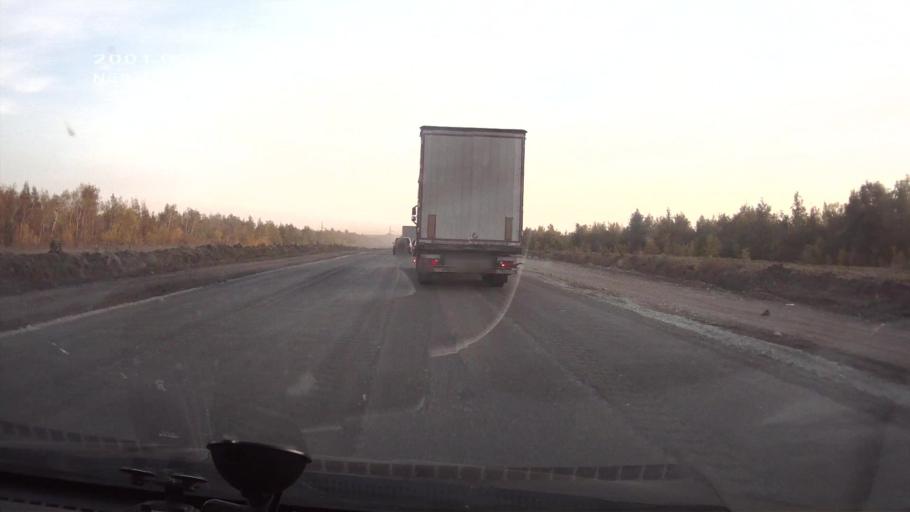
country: RU
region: Saratov
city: Kamenskiy
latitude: 50.9294
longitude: 45.5997
